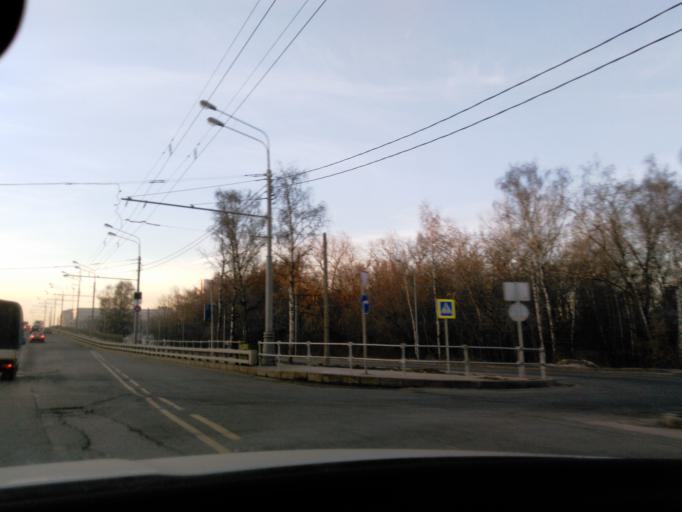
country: RU
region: Moskovskaya
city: Levoberezhnyy
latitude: 55.8269
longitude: 37.4910
